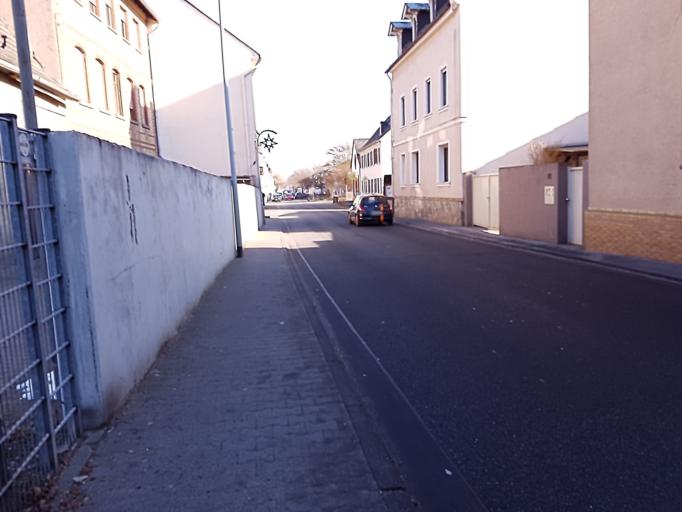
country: DE
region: Rheinland-Pfalz
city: Oestrich-Winkel
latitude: 50.0066
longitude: 8.0311
